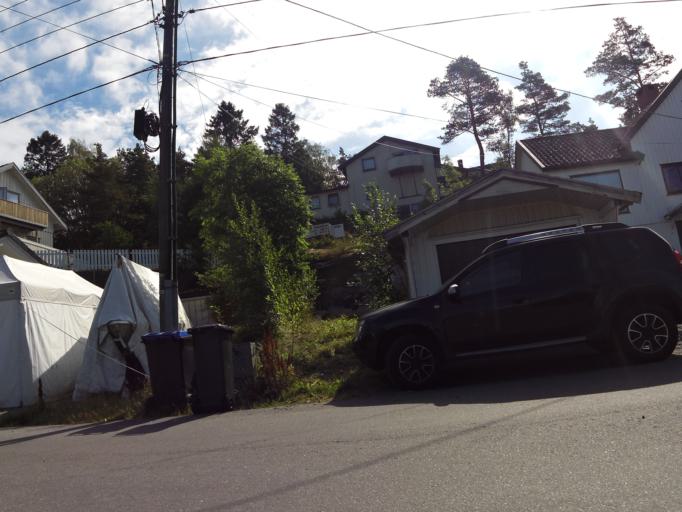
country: NO
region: Ostfold
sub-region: Fredrikstad
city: Fredrikstad
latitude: 59.2355
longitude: 10.9168
